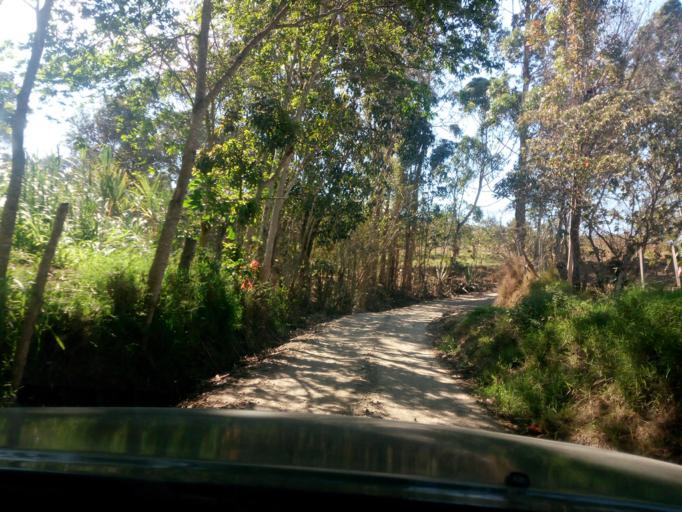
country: CO
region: Boyaca
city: Guateque
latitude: 4.9990
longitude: -73.4676
